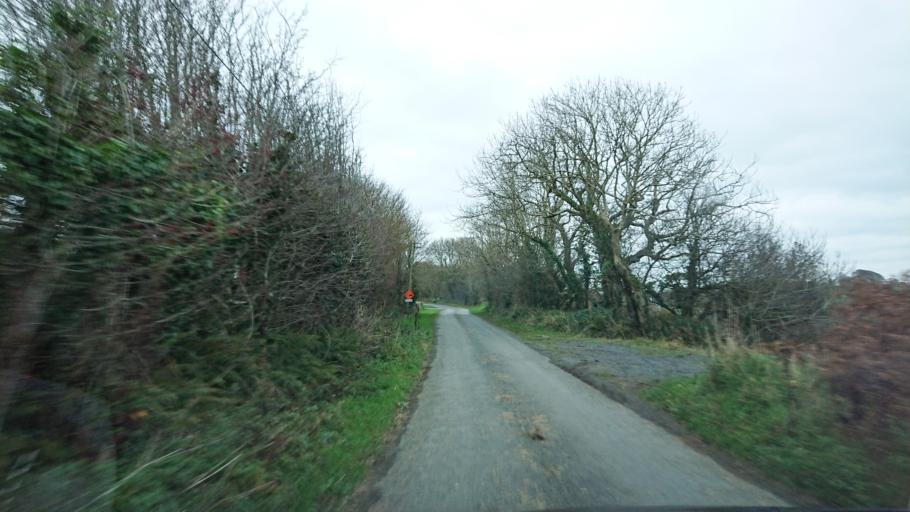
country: IE
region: Munster
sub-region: Waterford
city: Dunmore East
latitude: 52.1972
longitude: -7.0310
